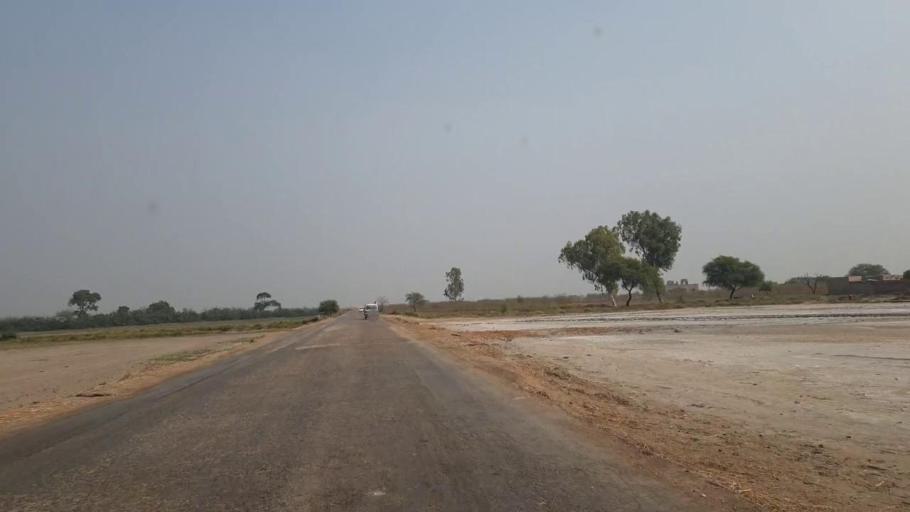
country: PK
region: Sindh
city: Matli
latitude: 25.0596
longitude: 68.6415
